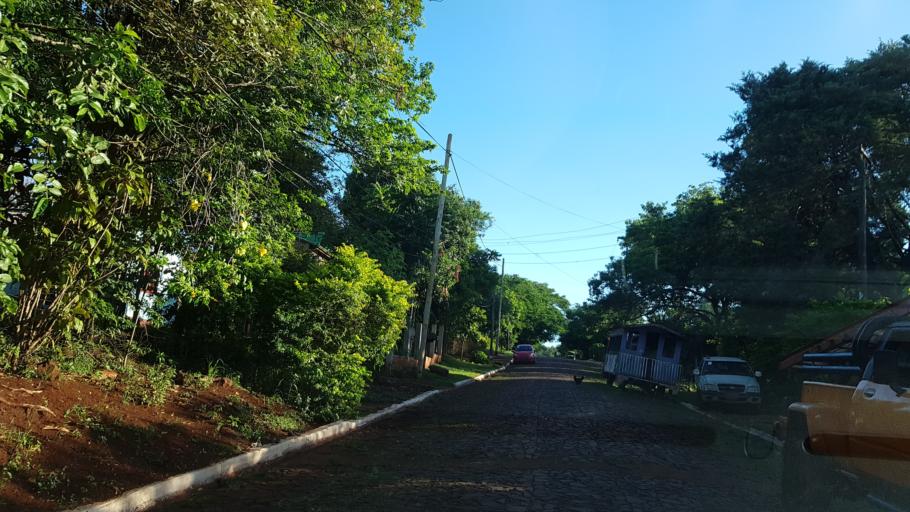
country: AR
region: Misiones
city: Puerto Libertad
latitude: -25.9200
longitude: -54.5870
